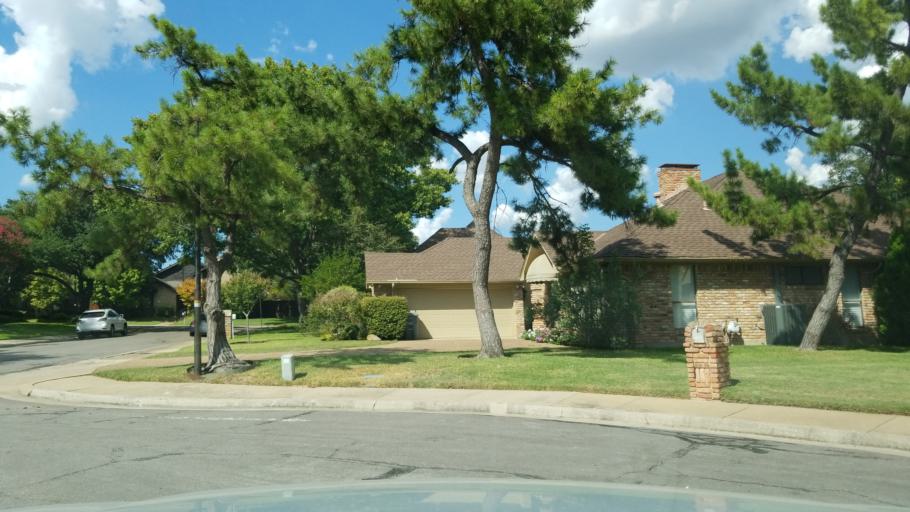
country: US
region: Texas
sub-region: Dallas County
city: Addison
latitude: 32.9534
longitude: -96.7988
